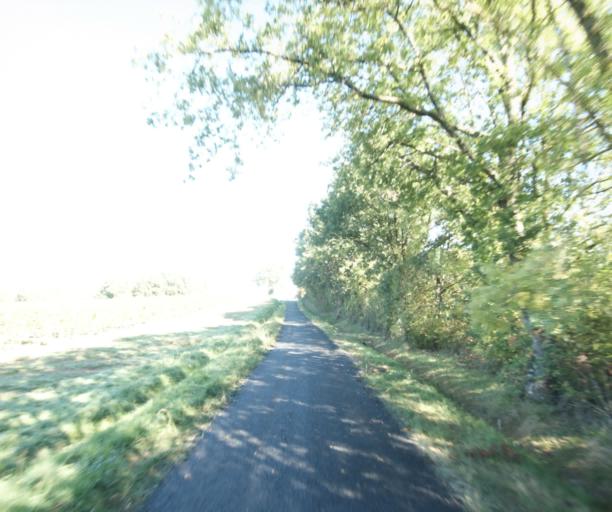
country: FR
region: Midi-Pyrenees
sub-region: Departement du Gers
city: Gondrin
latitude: 43.8130
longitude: 0.1951
